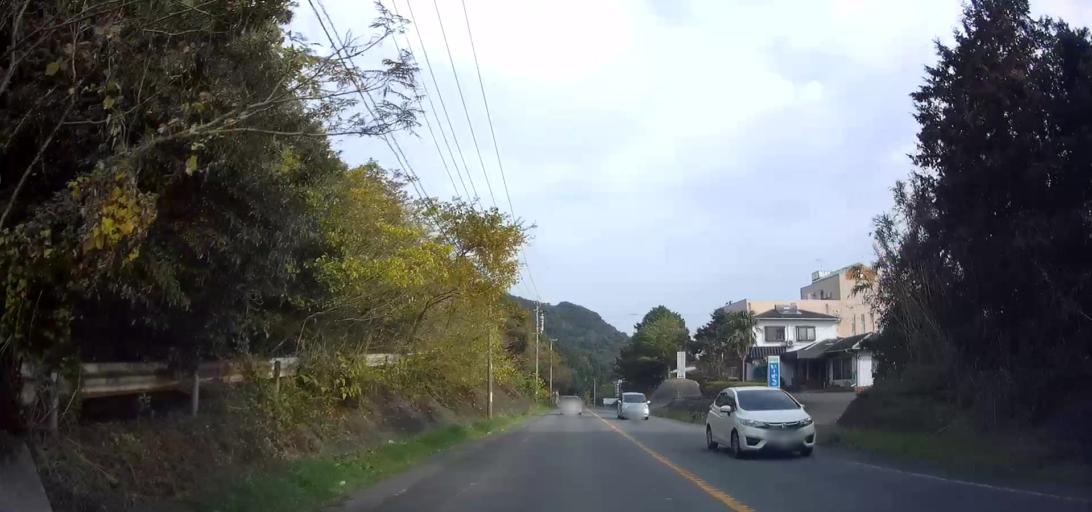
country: JP
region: Nagasaki
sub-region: Isahaya-shi
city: Isahaya
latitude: 32.7964
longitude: 130.1236
